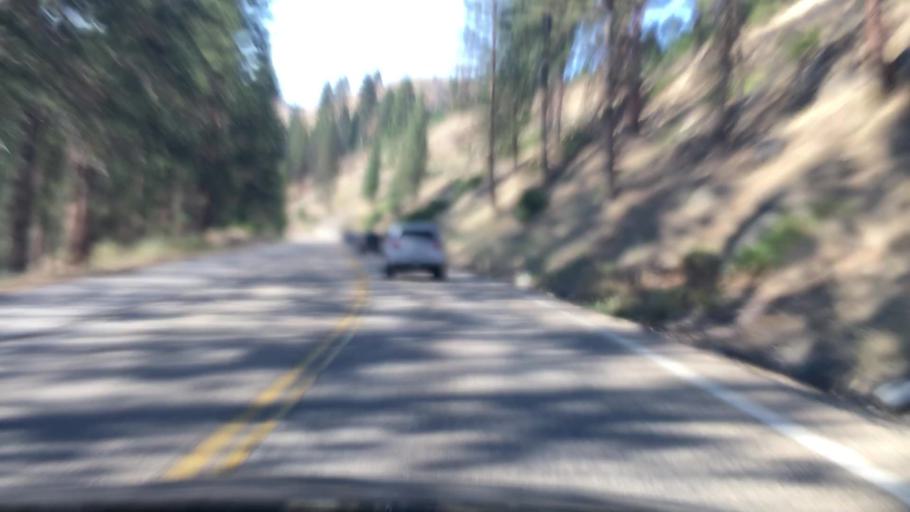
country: US
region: Idaho
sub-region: Boise County
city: Idaho City
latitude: 44.0700
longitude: -116.1187
